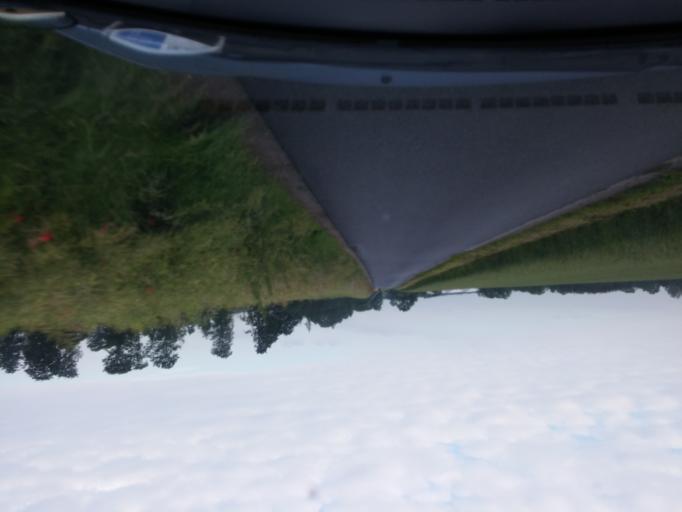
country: DK
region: South Denmark
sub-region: Kerteminde Kommune
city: Munkebo
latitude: 55.4081
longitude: 10.5628
